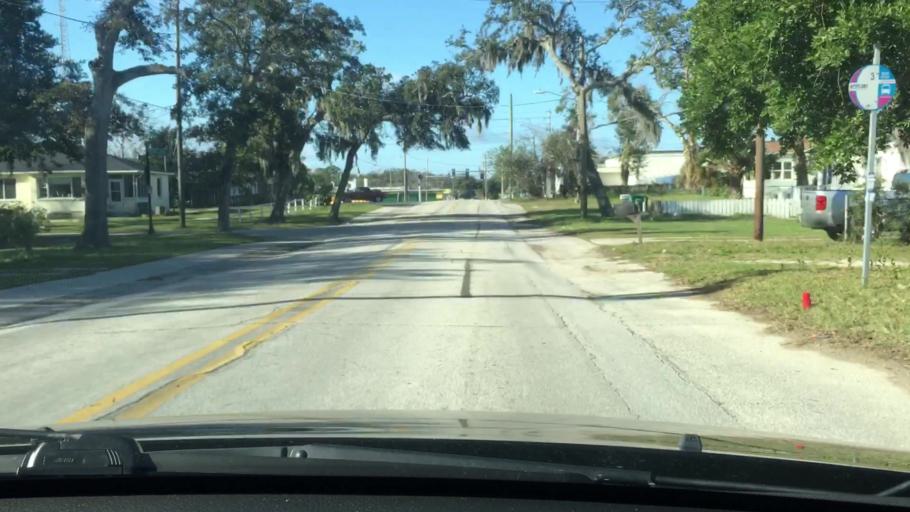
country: US
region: Florida
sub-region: Volusia County
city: Holly Hill
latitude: 29.2298
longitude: -81.0310
